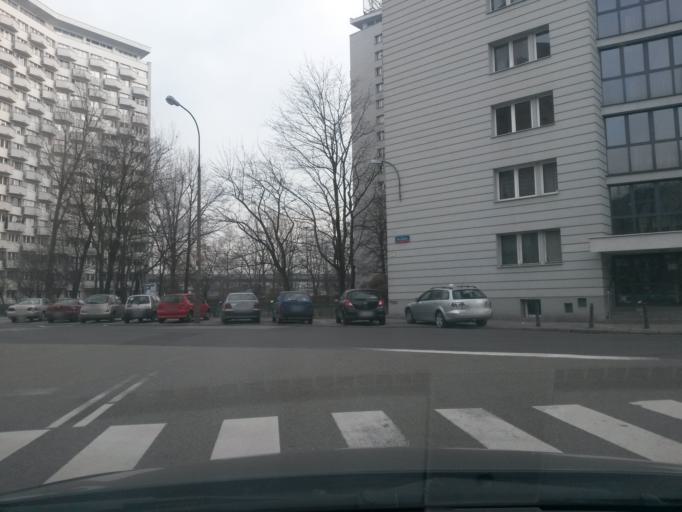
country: PL
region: Masovian Voivodeship
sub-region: Warszawa
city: Srodmiescie
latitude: 52.2259
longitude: 21.0404
